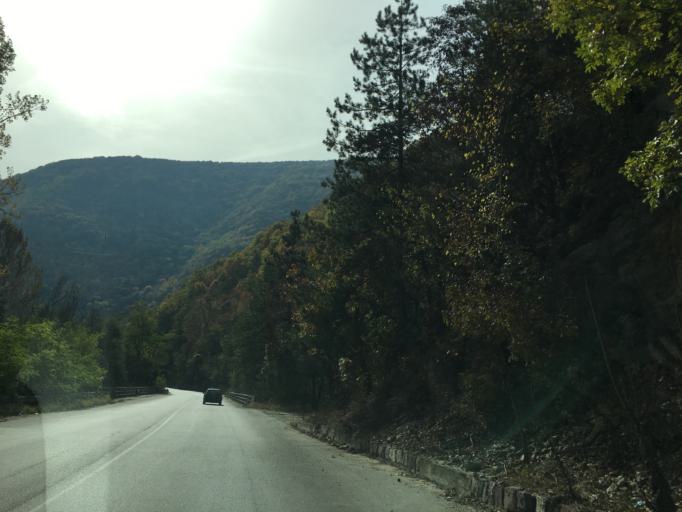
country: BG
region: Sofia-Capital
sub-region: Stolichna Obshtina
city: Sofia
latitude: 42.5608
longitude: 23.4227
